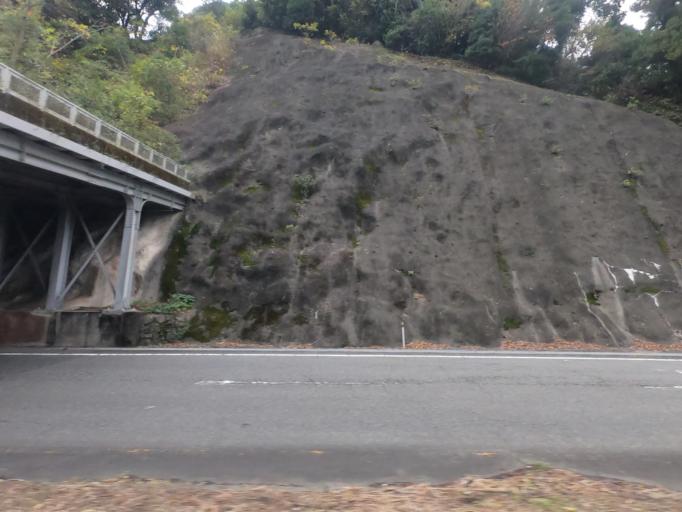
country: JP
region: Kumamoto
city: Minamata
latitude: 32.2439
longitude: 130.4848
